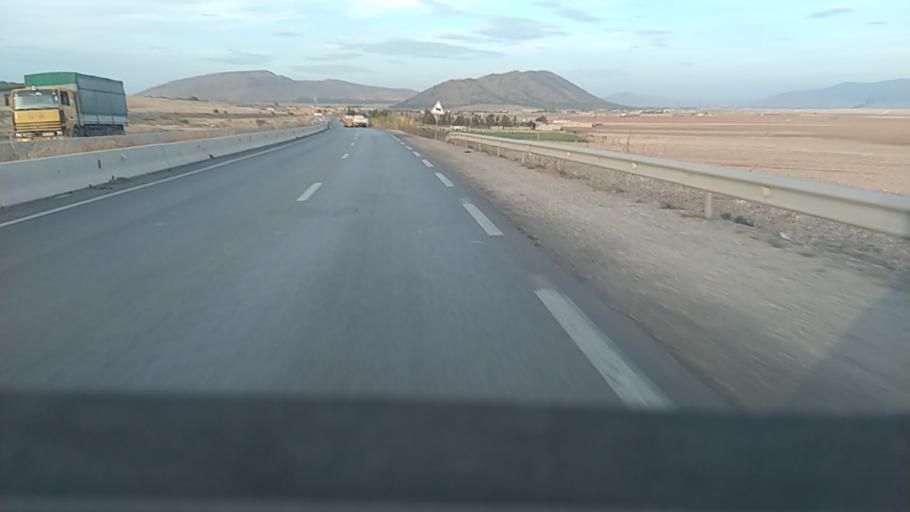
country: DZ
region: Oum el Bouaghi
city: Ain Kercha
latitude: 35.9454
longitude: 6.5231
